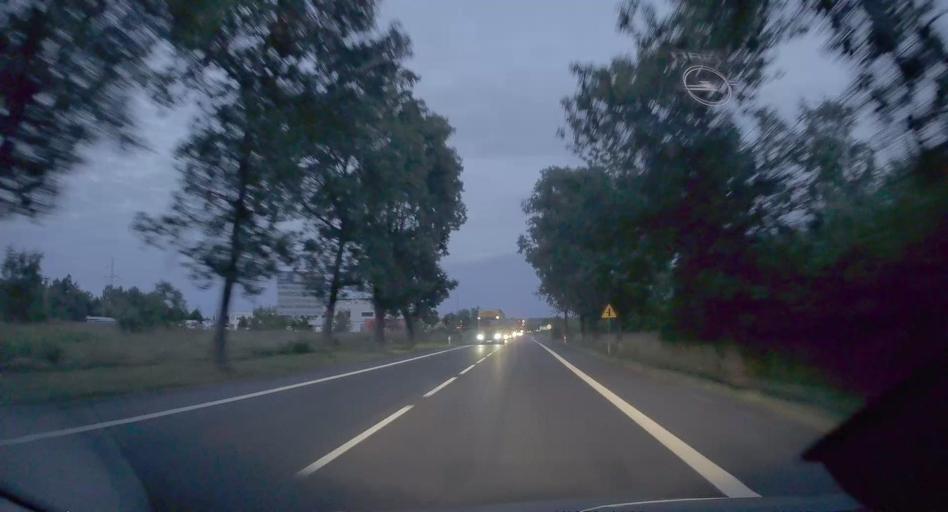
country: PL
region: Silesian Voivodeship
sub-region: Powiat klobucki
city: Klobuck
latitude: 50.9081
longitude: 18.9148
